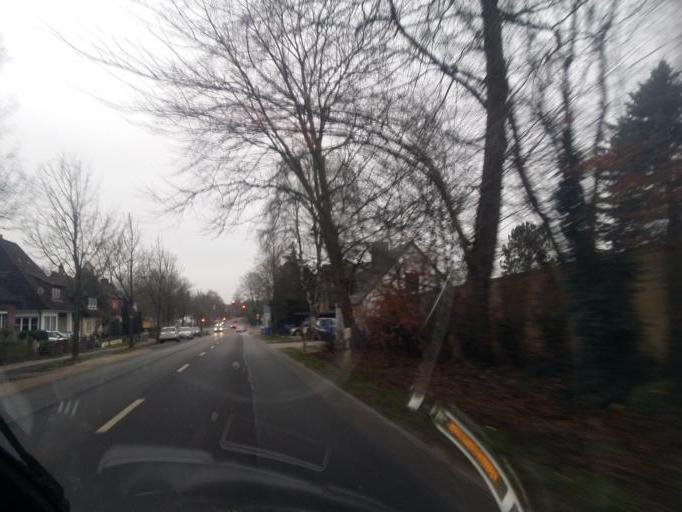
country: DE
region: Schleswig-Holstein
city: Heide
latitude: 54.2081
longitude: 9.1095
